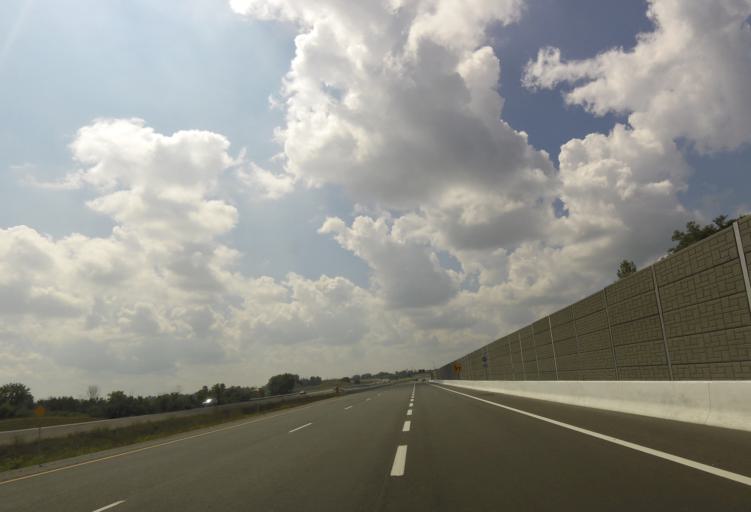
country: CA
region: Ontario
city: Oshawa
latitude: 43.9491
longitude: -78.9493
